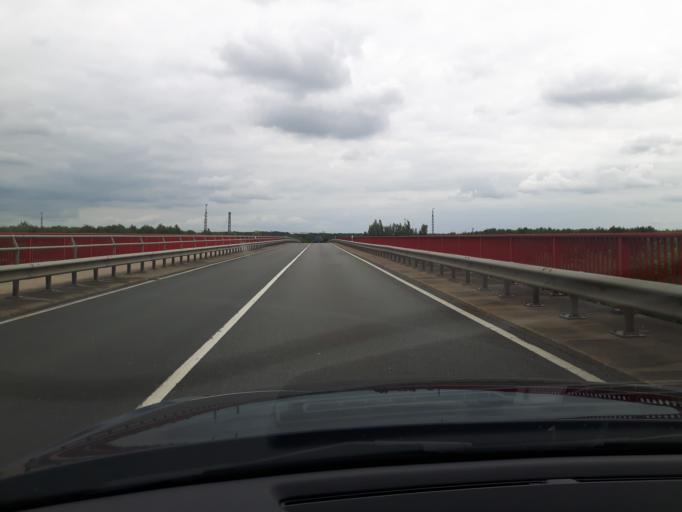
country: DE
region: Lower Saxony
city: Lehrte
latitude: 52.3804
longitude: 9.9468
